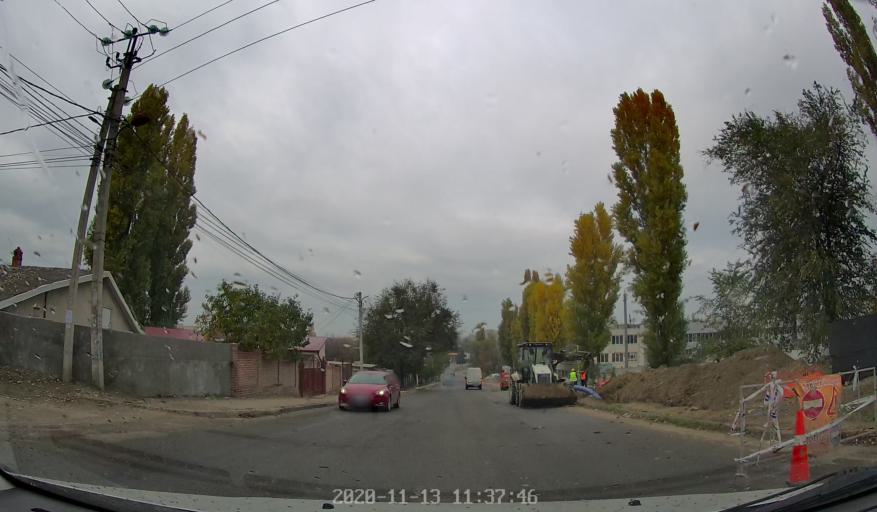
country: MD
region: Chisinau
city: Chisinau
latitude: 46.9926
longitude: 28.9103
